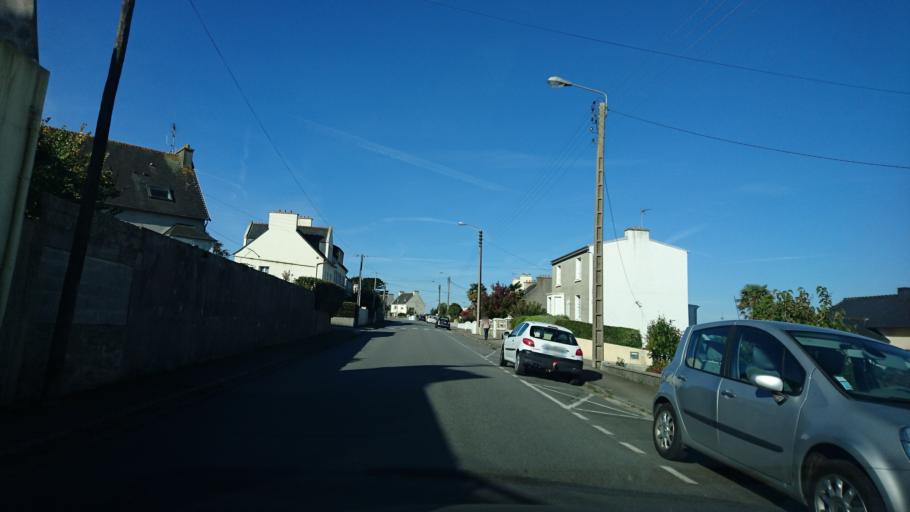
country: FR
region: Brittany
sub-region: Departement du Finistere
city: Saint-Renan
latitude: 48.4323
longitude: -4.6269
